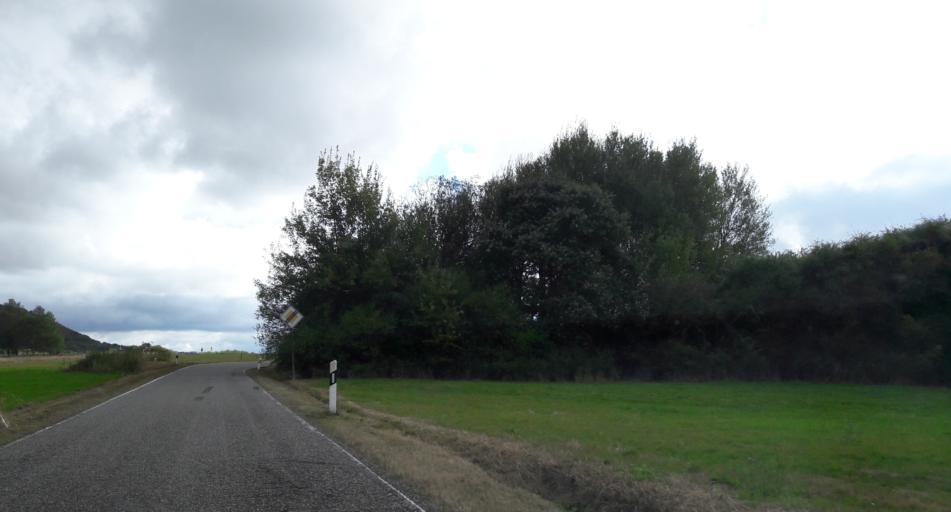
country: DE
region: Saarland
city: Freisen
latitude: 49.5275
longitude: 7.2227
